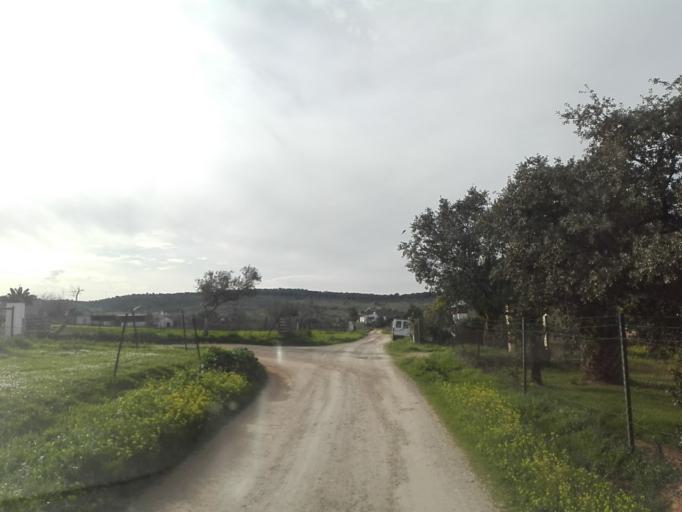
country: ES
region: Extremadura
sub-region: Provincia de Badajoz
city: Llerena
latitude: 38.2222
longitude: -6.0337
